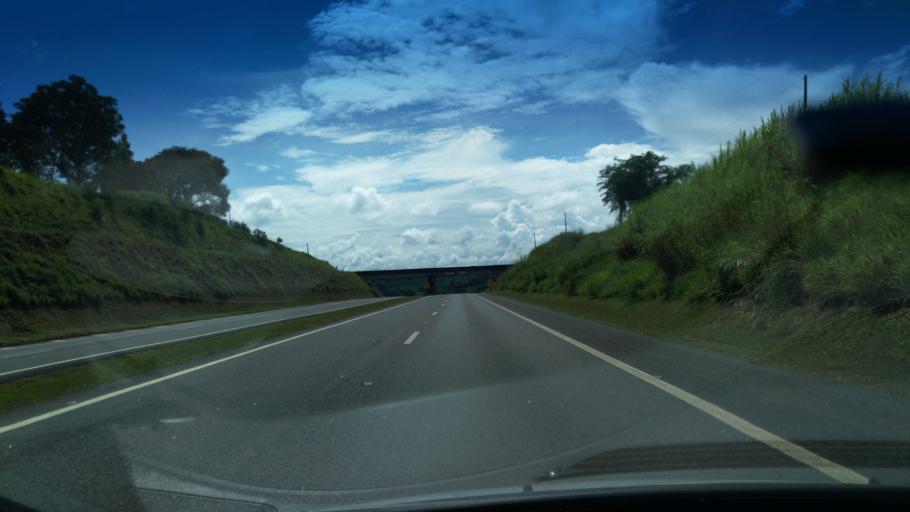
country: BR
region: Sao Paulo
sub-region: Santo Antonio Do Jardim
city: Espirito Santo do Pinhal
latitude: -22.2416
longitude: -46.8026
